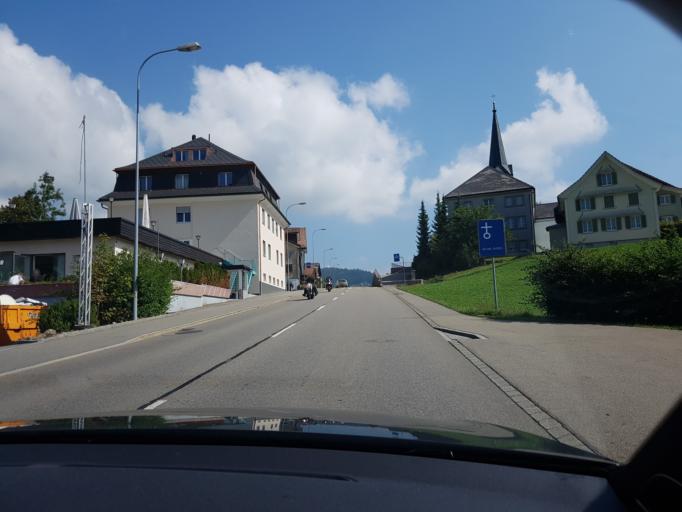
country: CH
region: Saint Gallen
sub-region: Wahlkreis See-Gaster
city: Gommiswald
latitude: 47.2646
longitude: 9.0454
